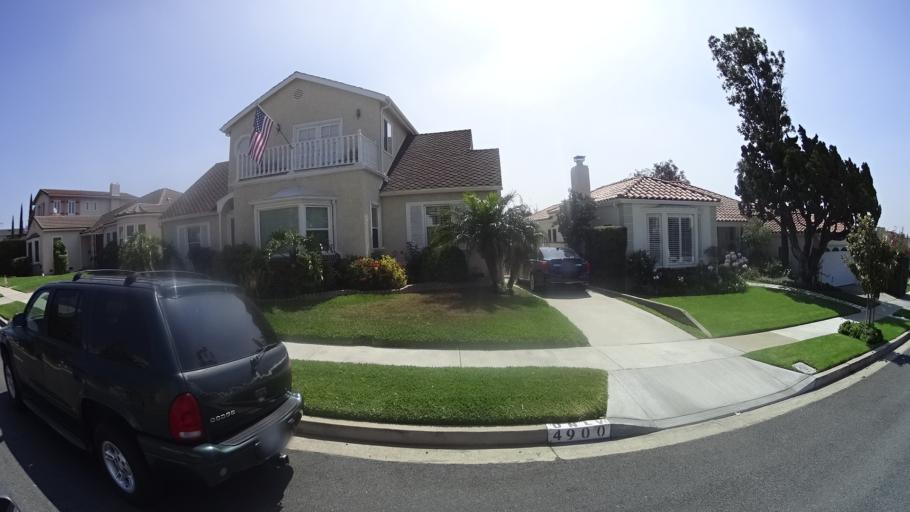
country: US
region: California
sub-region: Los Angeles County
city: View Park-Windsor Hills
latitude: 33.9979
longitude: -118.3450
